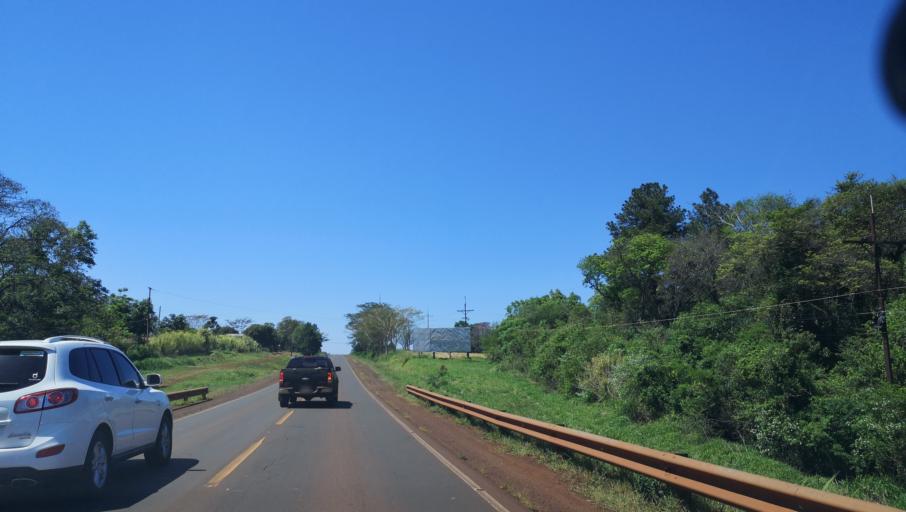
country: PY
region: Itapua
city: San Juan del Parana
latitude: -27.2599
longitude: -55.9662
